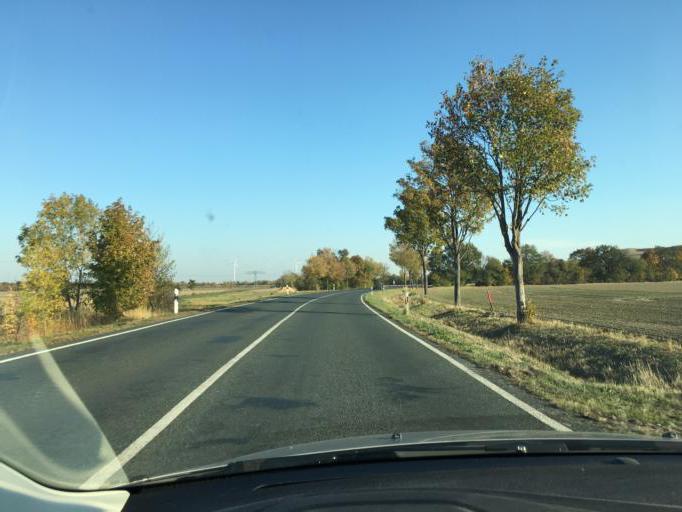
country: DE
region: Saxony
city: Rackwitz
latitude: 51.4186
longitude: 12.3916
